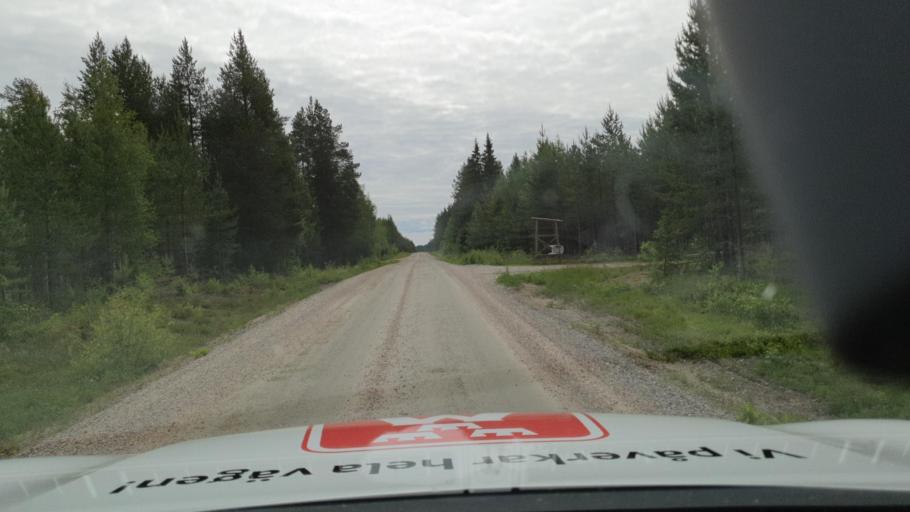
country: SE
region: Vaesterbotten
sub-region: Skelleftea Kommun
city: Forsbacka
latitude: 64.6451
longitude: 20.4544
